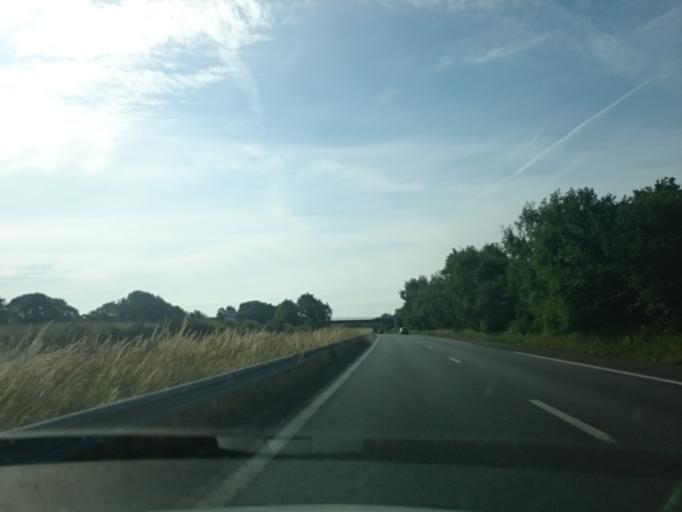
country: FR
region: Brittany
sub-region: Departement du Morbihan
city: Gestel
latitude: 47.7944
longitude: -3.4508
